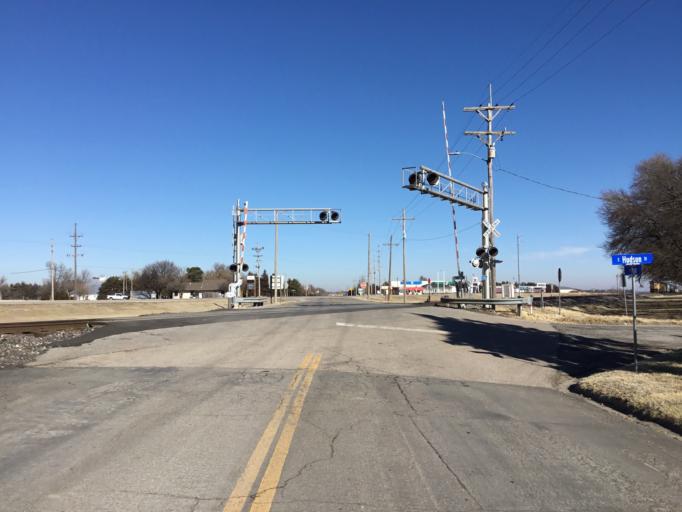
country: US
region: Kansas
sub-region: McPherson County
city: Inman
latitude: 38.2337
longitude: -97.7758
